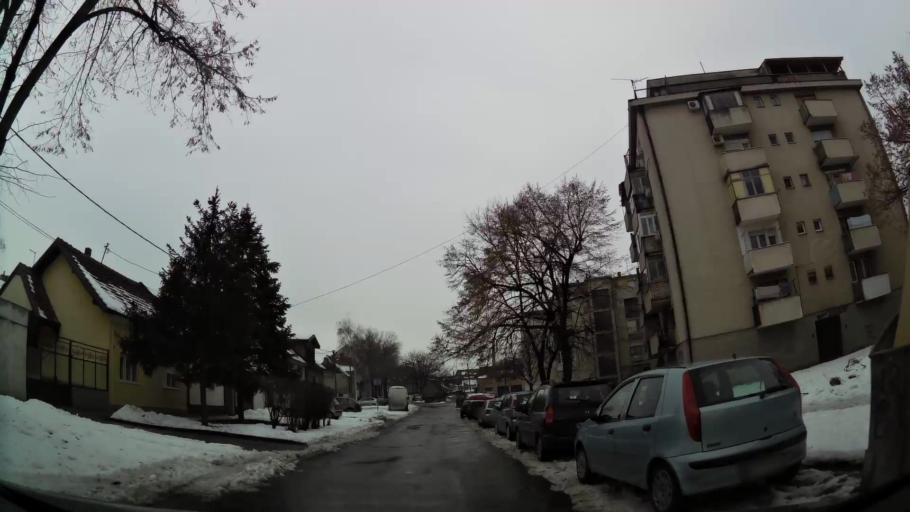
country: RS
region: Central Serbia
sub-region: Belgrade
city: Zemun
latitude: 44.8521
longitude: 20.3909
